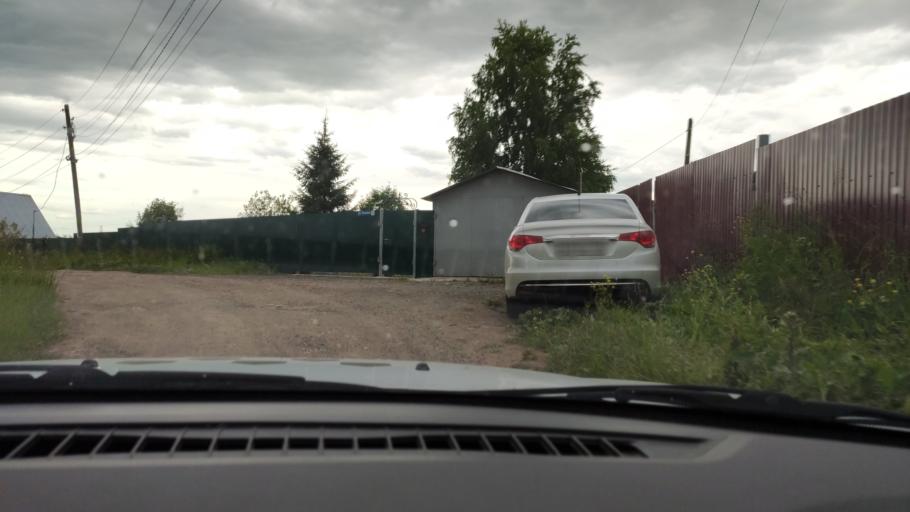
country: RU
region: Perm
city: Ferma
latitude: 57.9372
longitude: 56.3272
